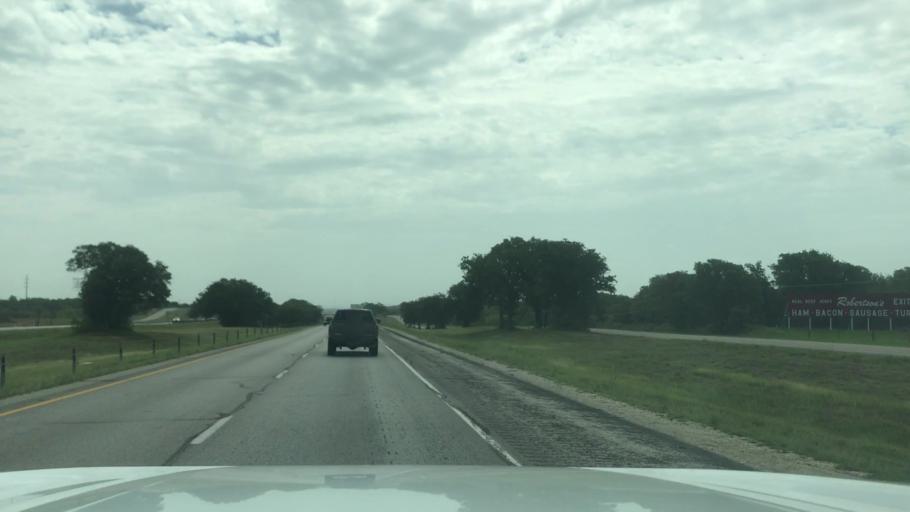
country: US
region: Texas
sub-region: Callahan County
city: Baird
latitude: 32.4054
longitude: -99.4385
